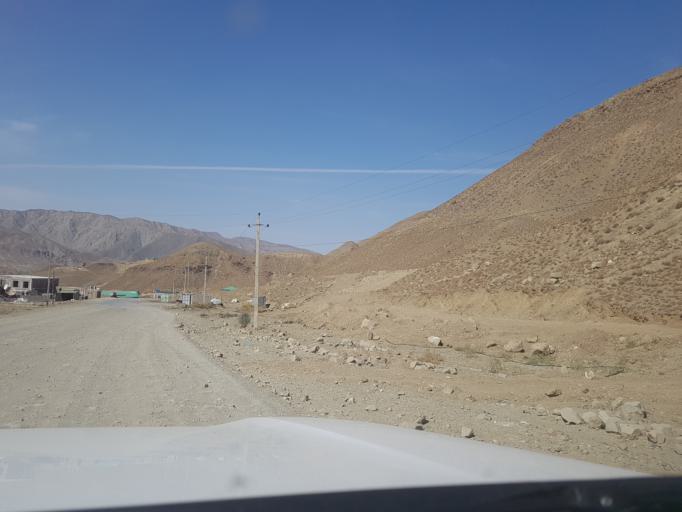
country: TM
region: Ahal
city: Baharly
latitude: 38.4538
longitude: 57.0450
